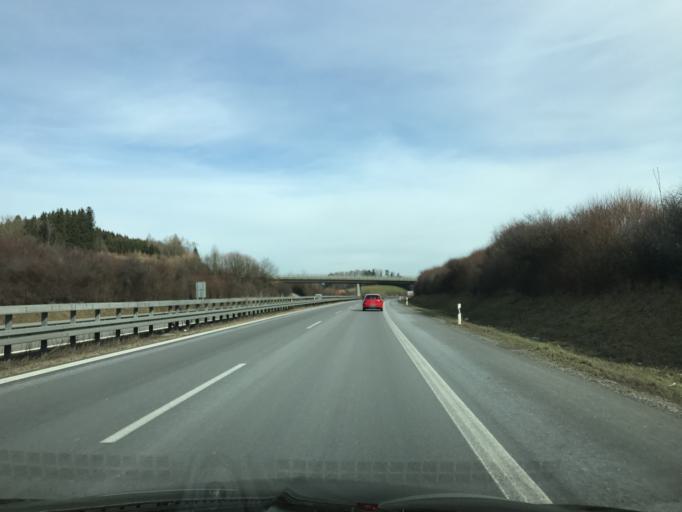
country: DE
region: Baden-Wuerttemberg
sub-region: Tuebingen Region
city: Amtzell
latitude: 47.6859
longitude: 9.7864
